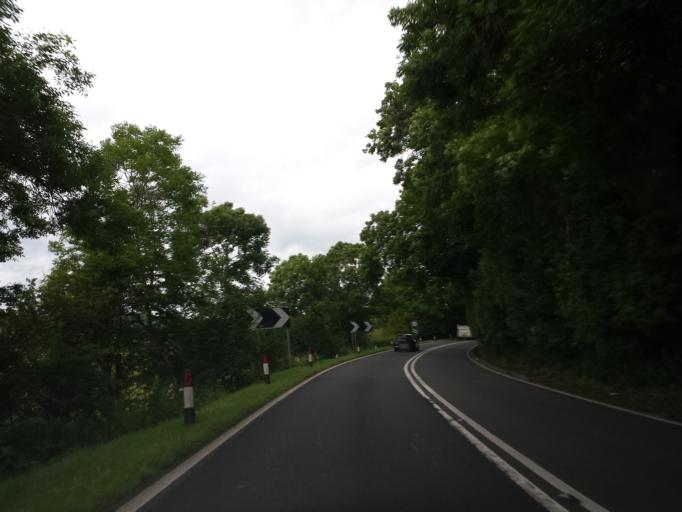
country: GB
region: Scotland
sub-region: Dumfries and Galloway
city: Dalbeattie
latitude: 55.0324
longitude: -3.8346
